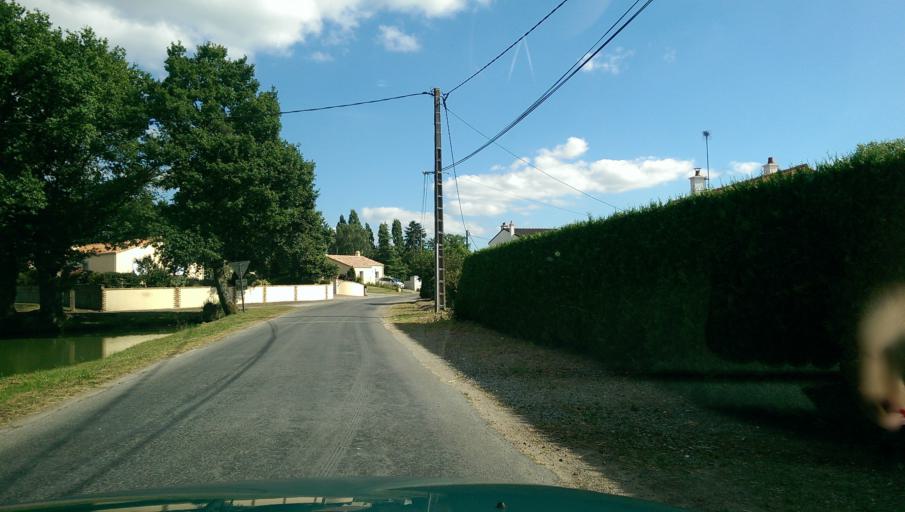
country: FR
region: Pays de la Loire
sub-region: Departement de la Loire-Atlantique
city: Lege
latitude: 46.9019
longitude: -1.5664
